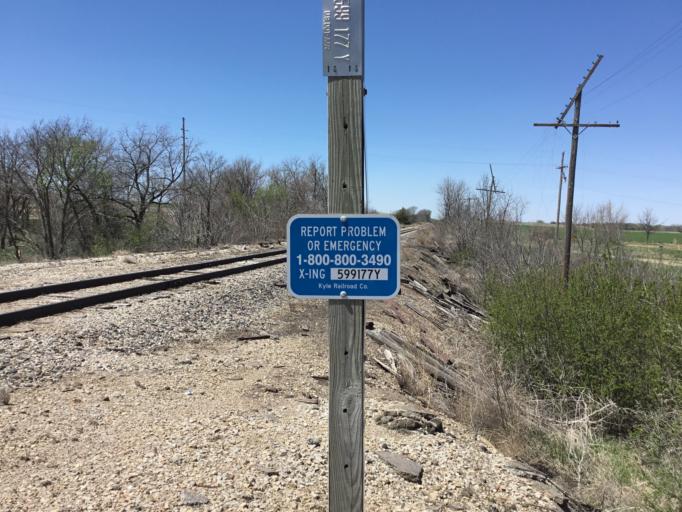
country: US
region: Kansas
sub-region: Phillips County
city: Phillipsburg
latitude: 39.7993
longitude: -99.4593
